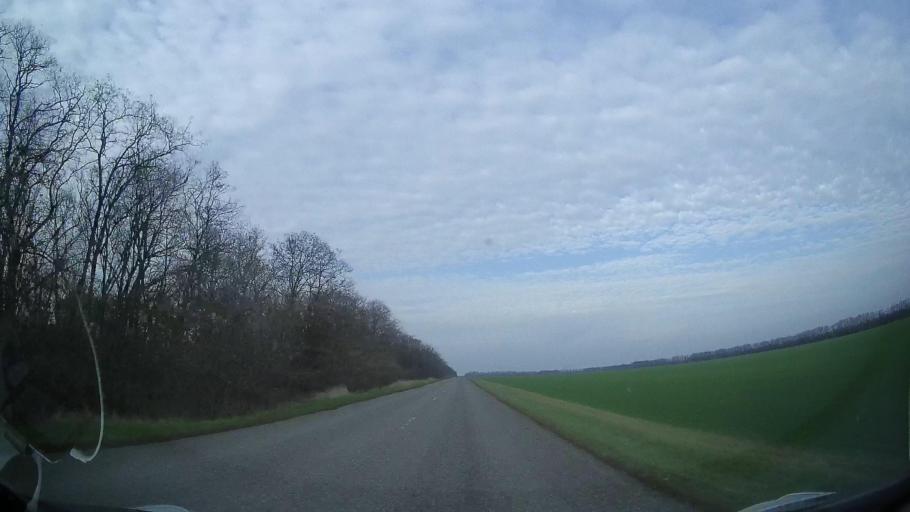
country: RU
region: Rostov
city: Zernograd
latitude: 46.9710
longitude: 40.3916
